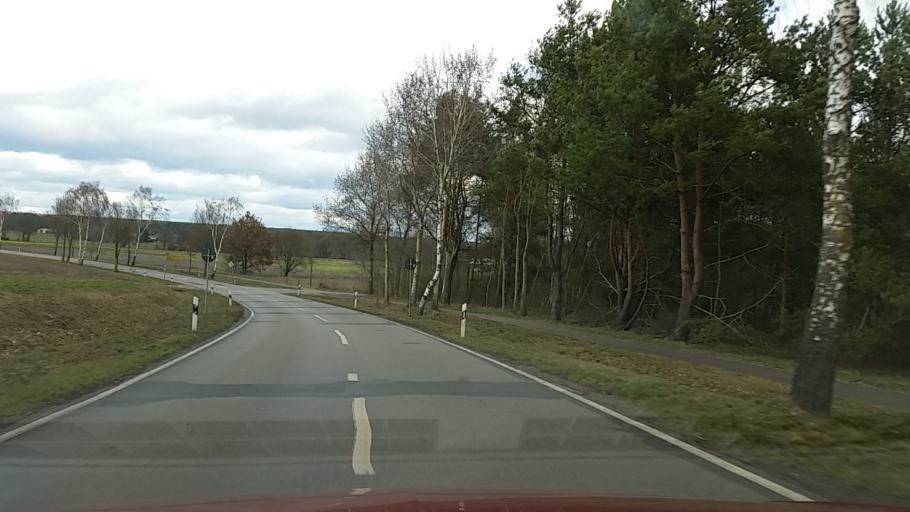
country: DE
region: Lower Saxony
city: Karwitz
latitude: 53.0403
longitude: 11.0063
